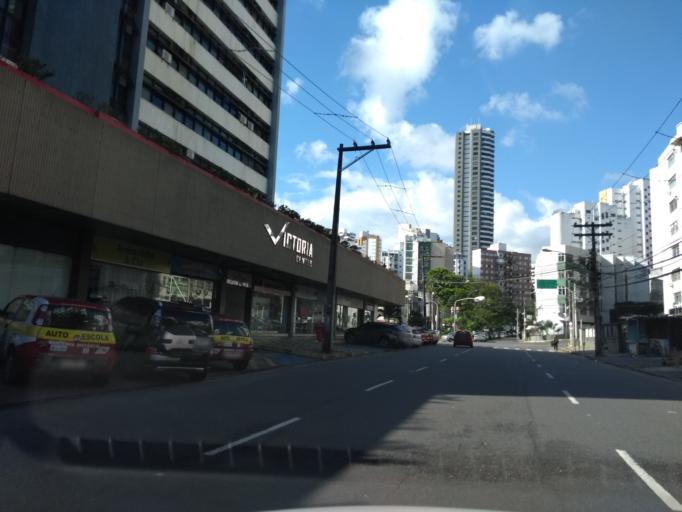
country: BR
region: Bahia
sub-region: Salvador
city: Salvador
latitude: -13.0063
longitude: -38.5228
